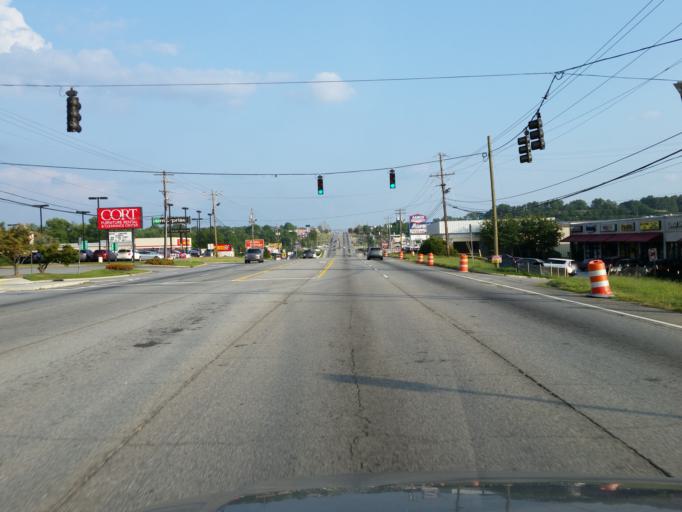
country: US
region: Georgia
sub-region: Cobb County
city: Smyrna
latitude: 33.9126
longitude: -84.4964
